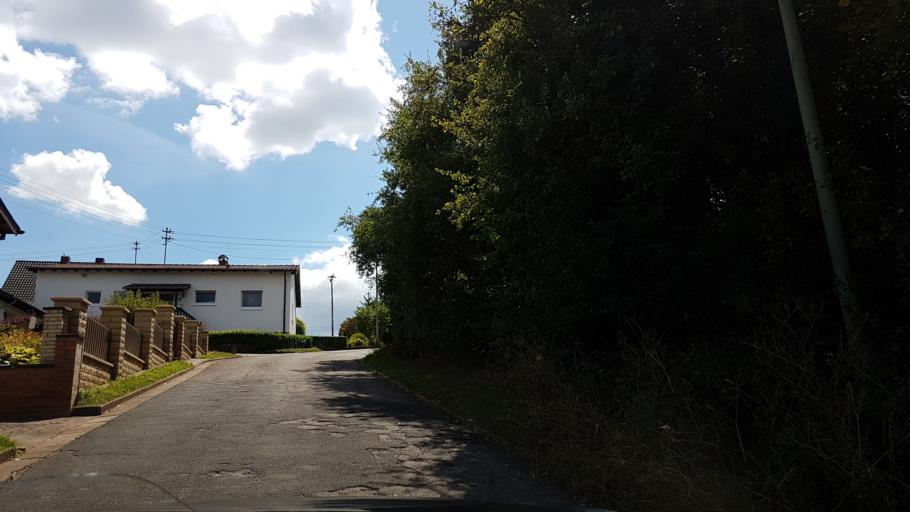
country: DE
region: Saarland
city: Illingen
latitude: 49.3744
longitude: 7.0408
